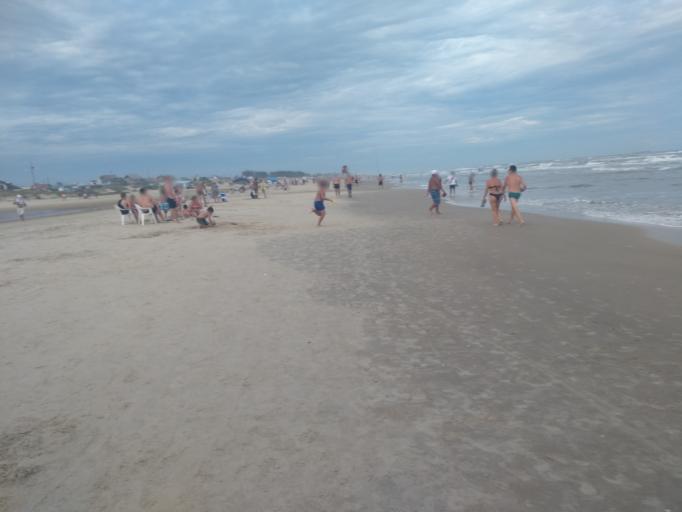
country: BR
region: Rio Grande do Sul
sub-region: Tramandai
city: Tramandai
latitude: -30.0594
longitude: -50.1549
